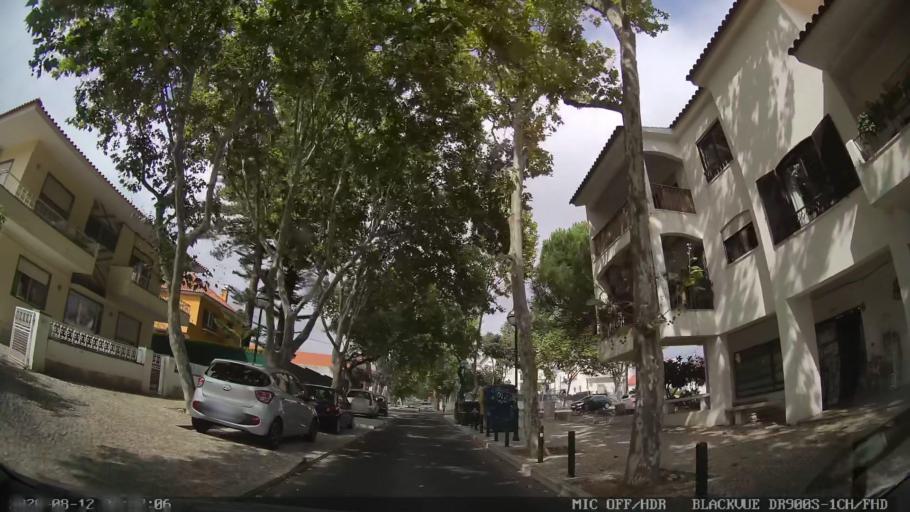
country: PT
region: Lisbon
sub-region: Cascais
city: Parede
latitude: 38.6960
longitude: -9.3730
